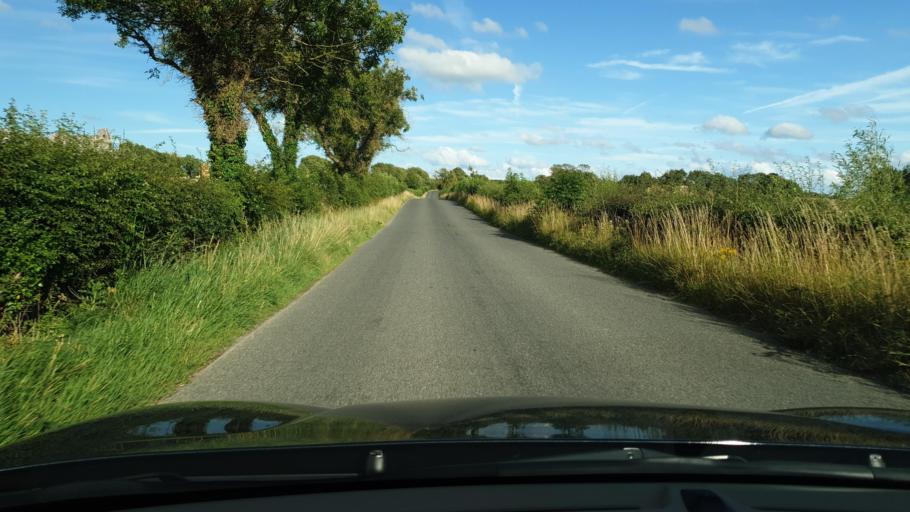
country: IE
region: Leinster
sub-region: An Mhi
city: Stamullin
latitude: 53.6229
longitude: -6.3361
